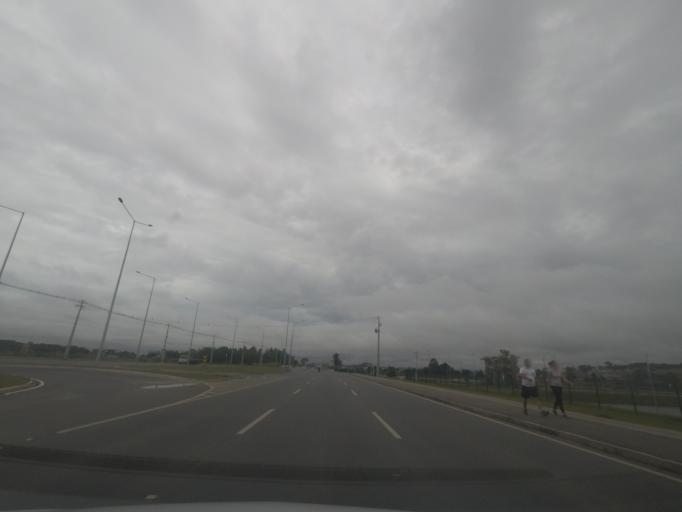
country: BR
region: Parana
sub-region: Pinhais
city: Pinhais
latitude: -25.4429
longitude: -49.1469
